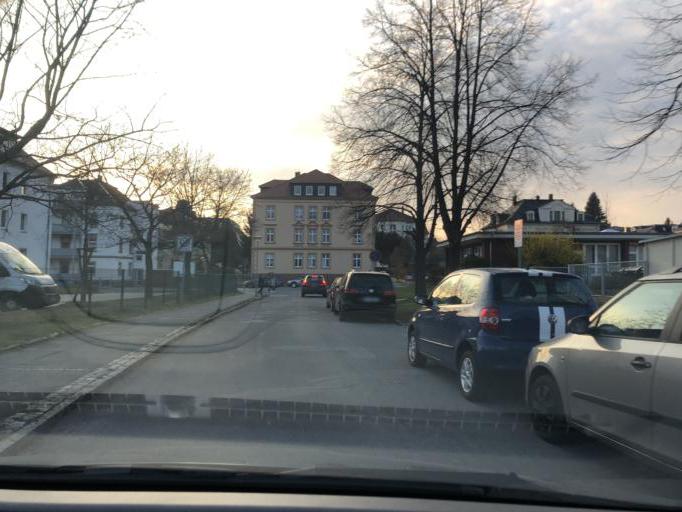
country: DE
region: Saxony
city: Bautzen
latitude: 51.1793
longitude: 14.4417
